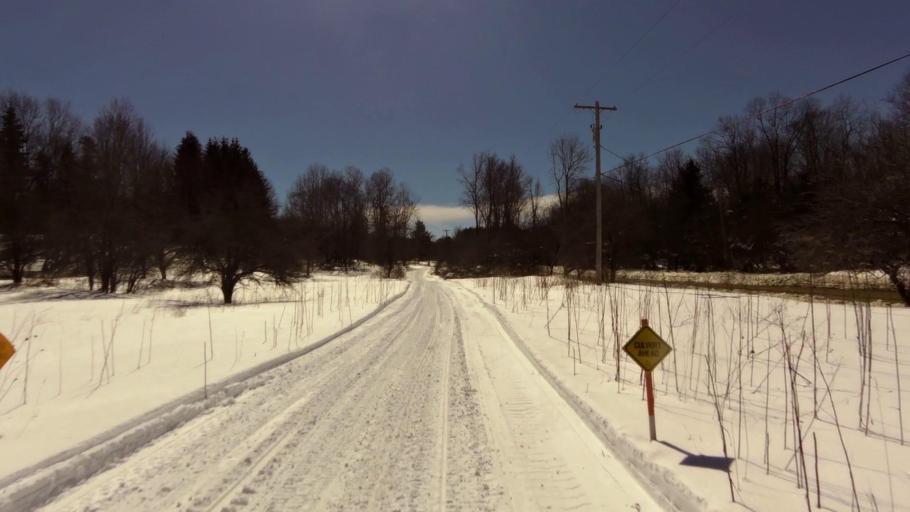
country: US
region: New York
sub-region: Allegany County
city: Cuba
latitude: 42.3327
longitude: -78.2499
